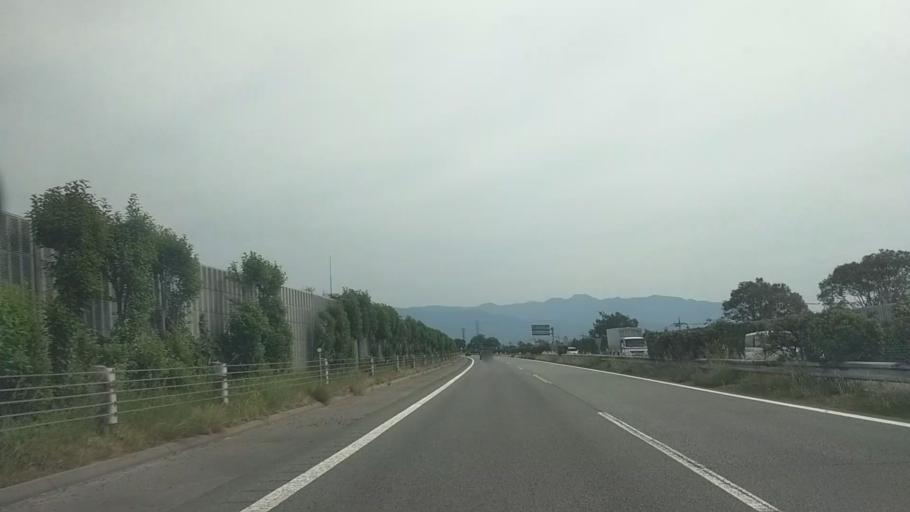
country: JP
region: Yamanashi
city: Kofu-shi
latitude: 35.6409
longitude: 138.5376
